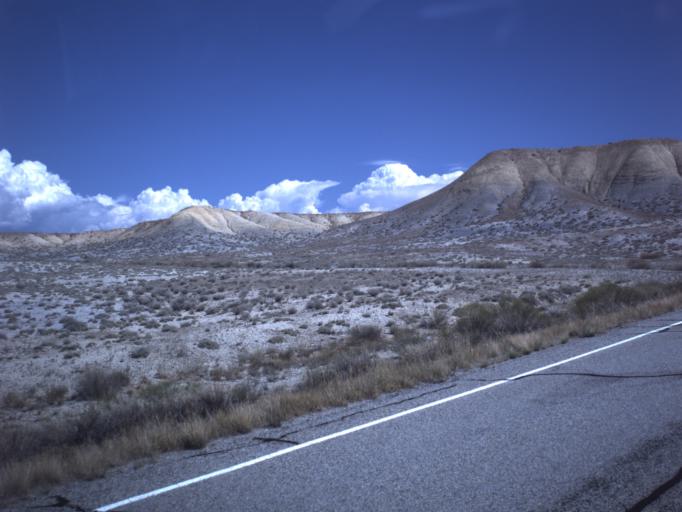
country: US
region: Utah
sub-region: Grand County
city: Moab
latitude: 38.9394
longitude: -109.3861
